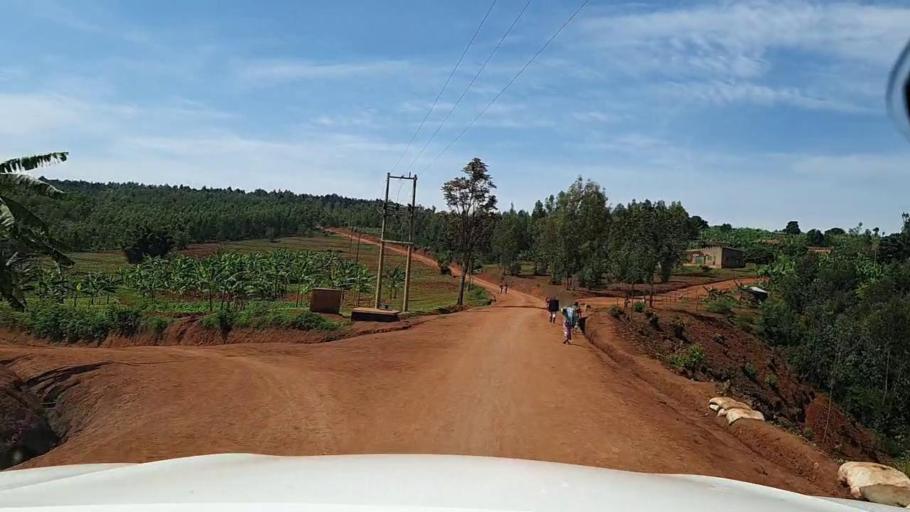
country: RW
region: Southern Province
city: Butare
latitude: -2.6991
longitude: 29.8545
